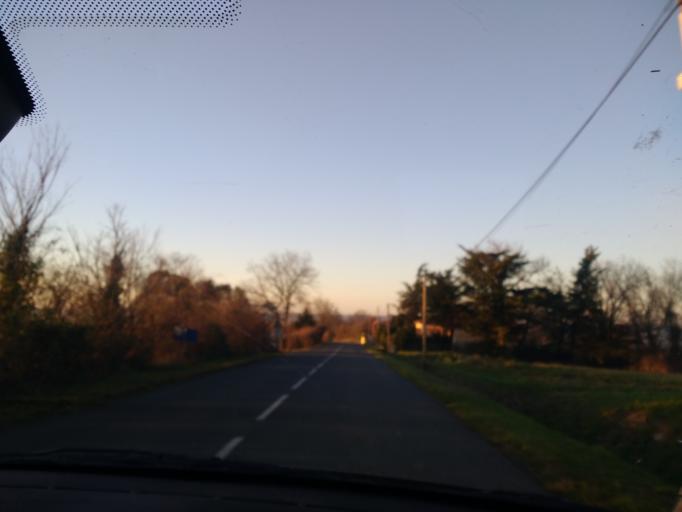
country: FR
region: Aquitaine
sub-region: Departement du Lot-et-Garonne
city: Castelmoron-sur-Lot
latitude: 44.3511
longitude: 0.5211
